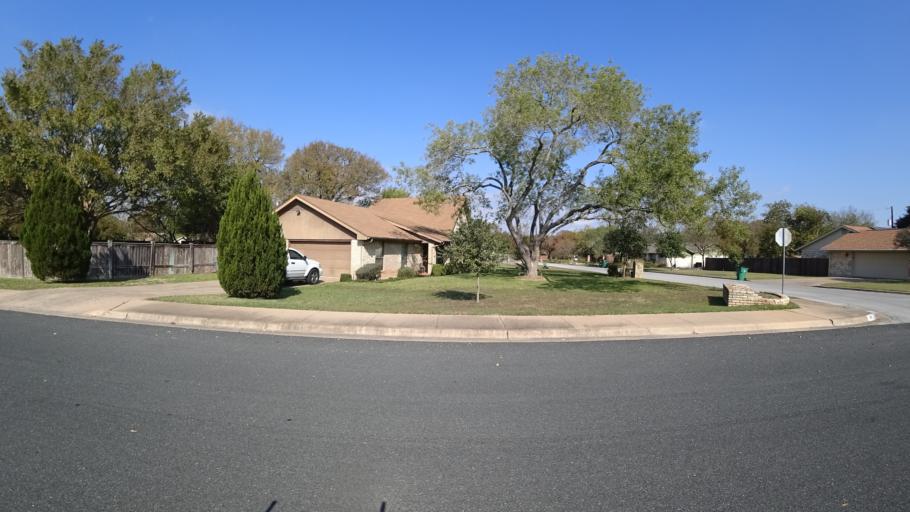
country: US
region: Texas
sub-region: Travis County
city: Shady Hollow
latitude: 30.1630
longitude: -97.8623
